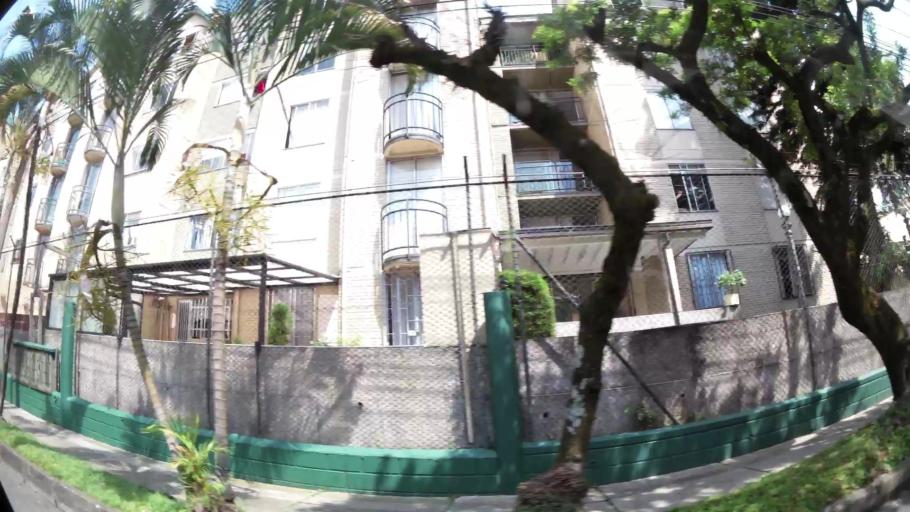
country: CO
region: Antioquia
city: Envigado
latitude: 6.1669
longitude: -75.5963
